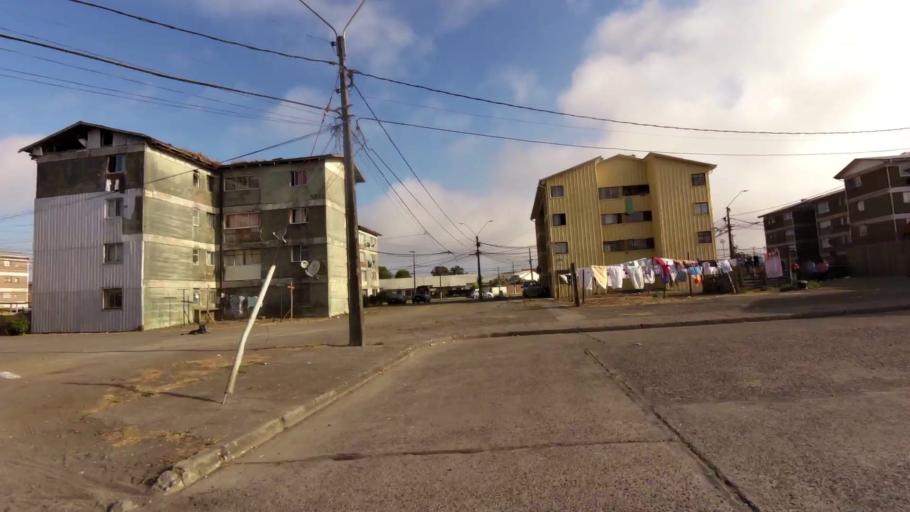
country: CL
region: Biobio
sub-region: Provincia de Concepcion
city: Concepcion
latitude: -36.7894
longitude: -73.0909
